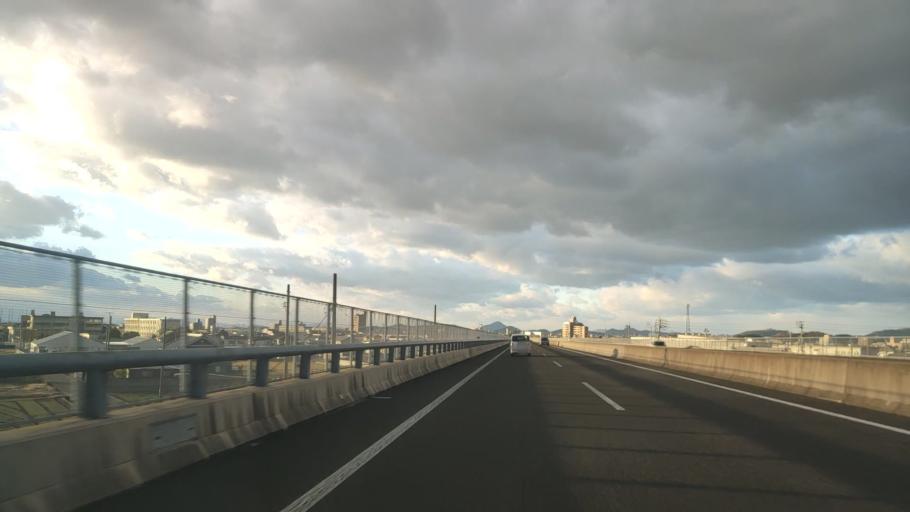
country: JP
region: Ehime
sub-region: Shikoku-chuo Shi
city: Matsuyama
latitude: 33.7918
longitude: 132.8026
